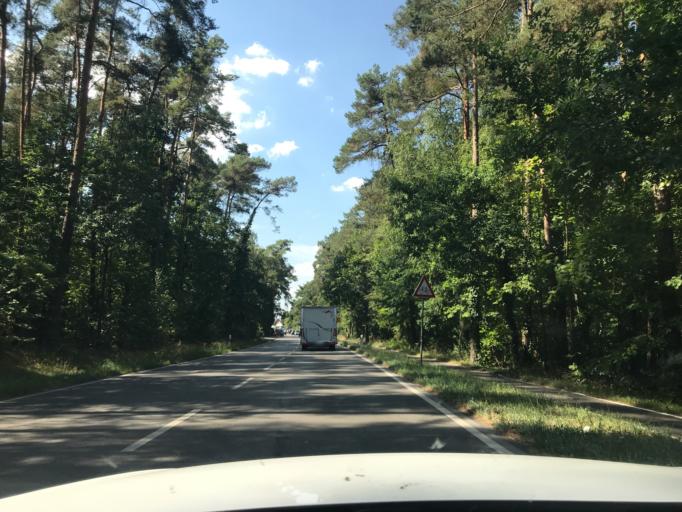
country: DE
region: Bavaria
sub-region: Regierungsbezirk Mittelfranken
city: Erlangen
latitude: 49.5633
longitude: 11.0080
